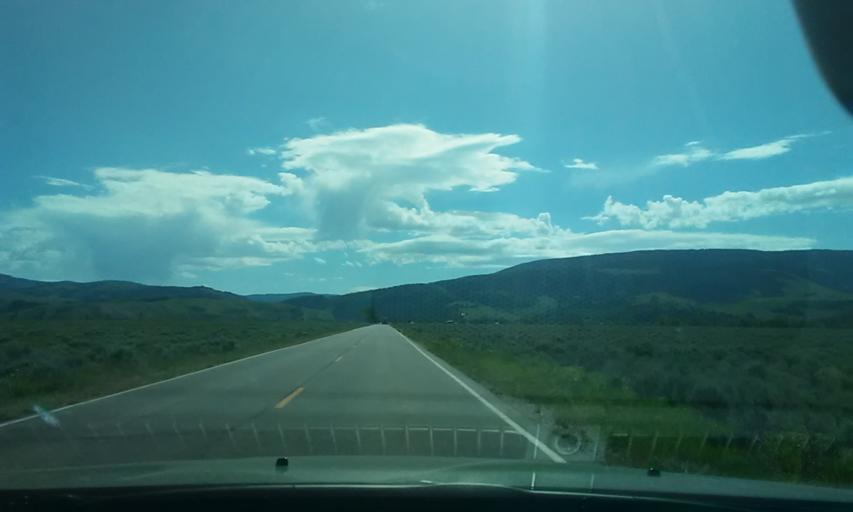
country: US
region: Wyoming
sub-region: Teton County
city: Jackson
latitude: 43.6251
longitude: -110.6476
